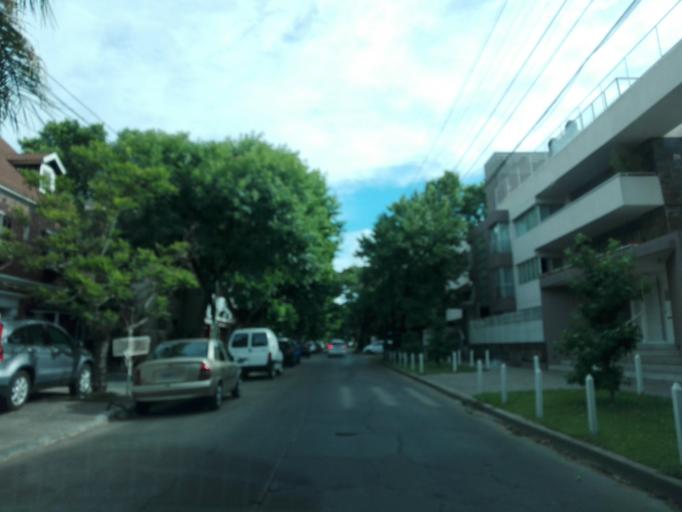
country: AR
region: Buenos Aires
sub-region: Partido de Lomas de Zamora
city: Lomas de Zamora
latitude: -34.7432
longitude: -58.3974
